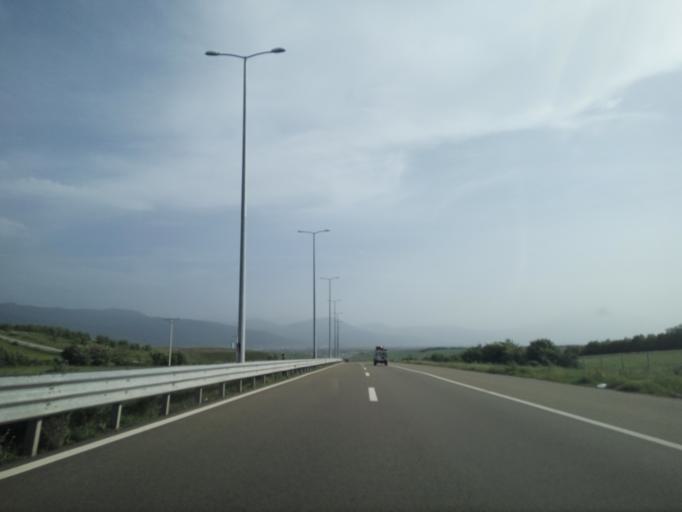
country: XK
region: Prizren
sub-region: Komuna e Therandes
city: Leshan
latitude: 42.3196
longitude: 20.7676
